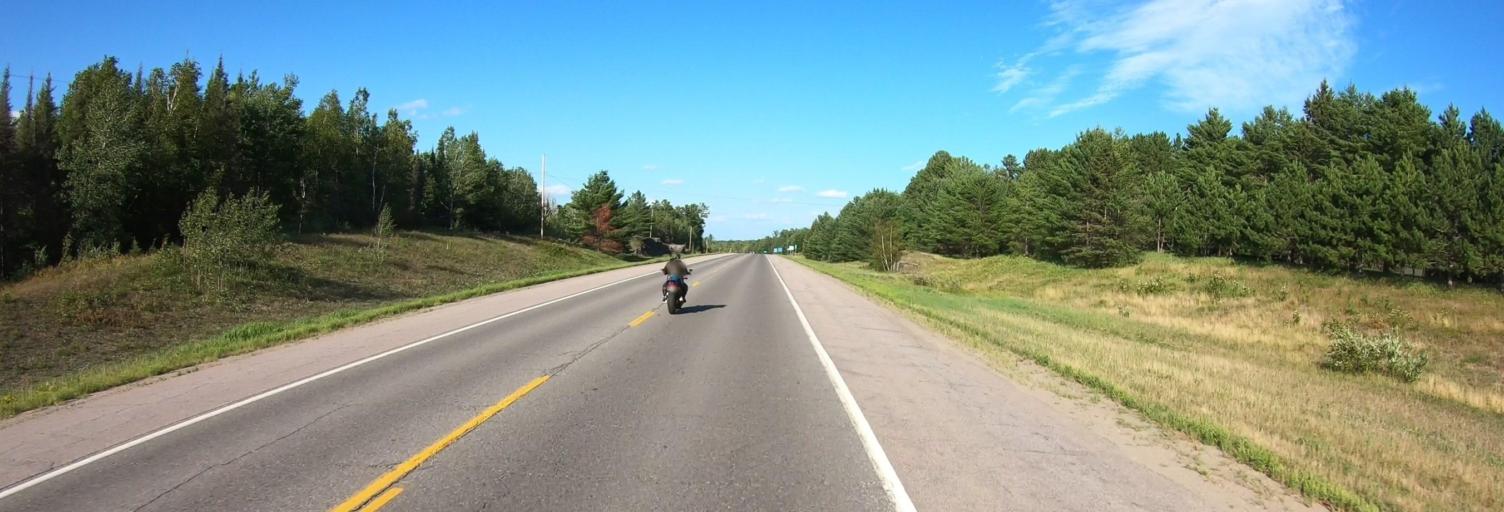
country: US
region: Minnesota
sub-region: Saint Louis County
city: Ely
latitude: 47.9105
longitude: -91.8186
